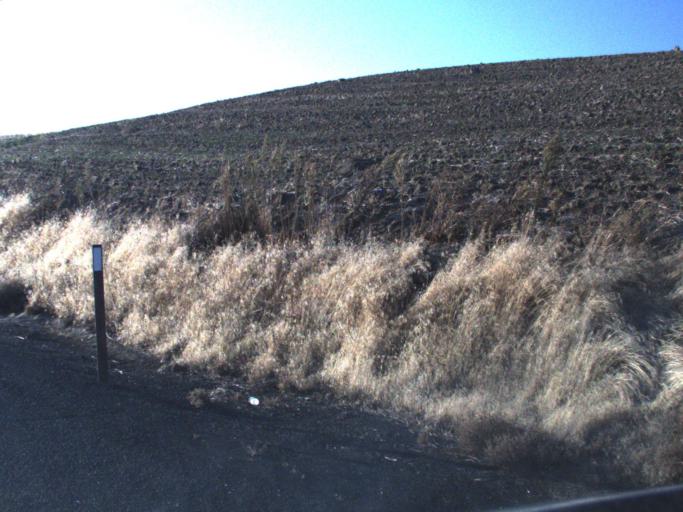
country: US
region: Washington
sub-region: Adams County
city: Ritzville
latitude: 46.6777
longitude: -118.3775
